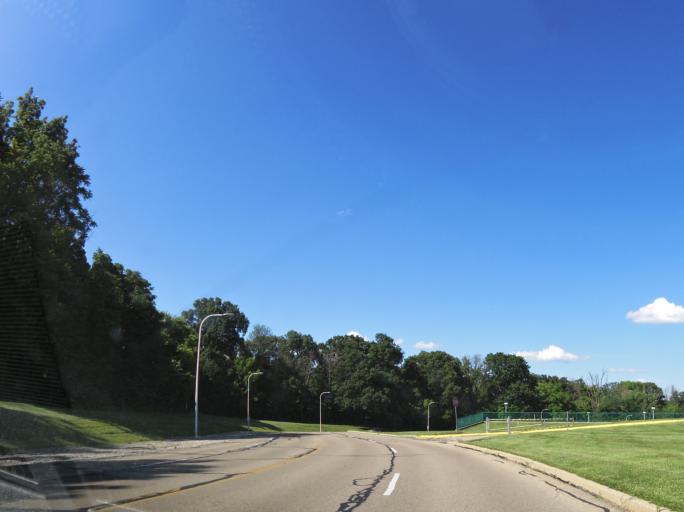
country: US
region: Ohio
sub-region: Greene County
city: Wright-Patterson AFB
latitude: 39.7829
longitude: -84.0539
